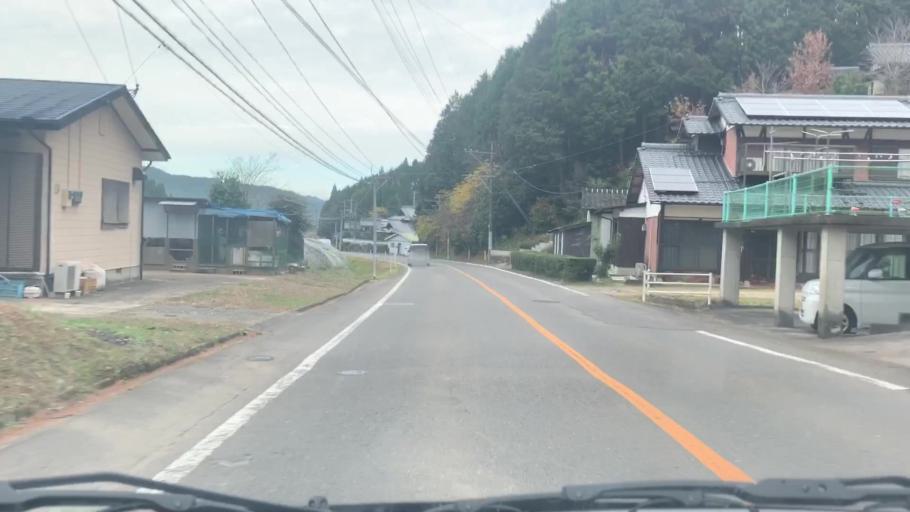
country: JP
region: Saga Prefecture
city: Takeocho-takeo
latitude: 33.1870
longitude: 129.9678
